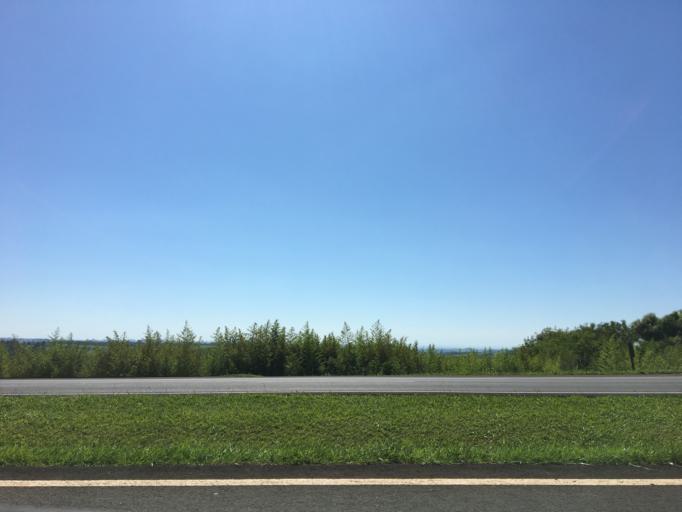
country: BR
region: Parana
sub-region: Rolandia
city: Rolandia
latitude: -23.3109
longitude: -51.3316
